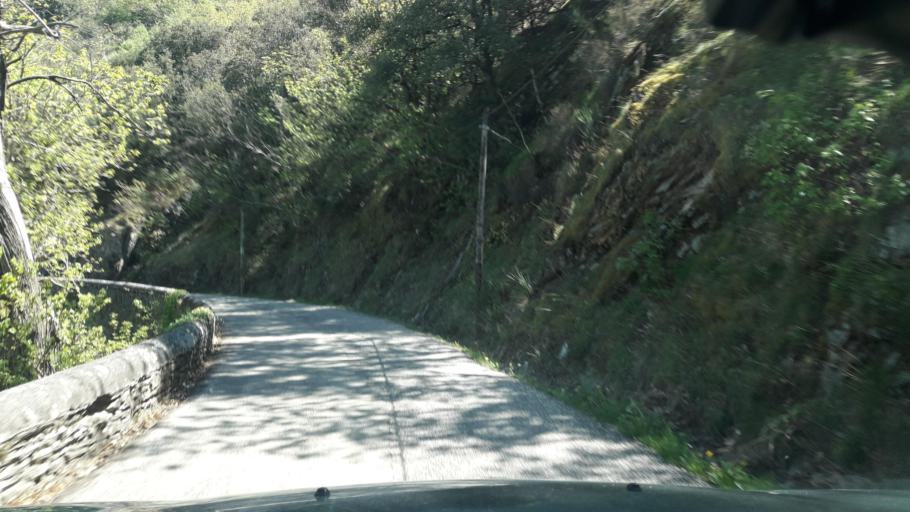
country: FR
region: Languedoc-Roussillon
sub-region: Departement du Gard
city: Valleraugue
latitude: 44.1113
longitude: 3.7059
